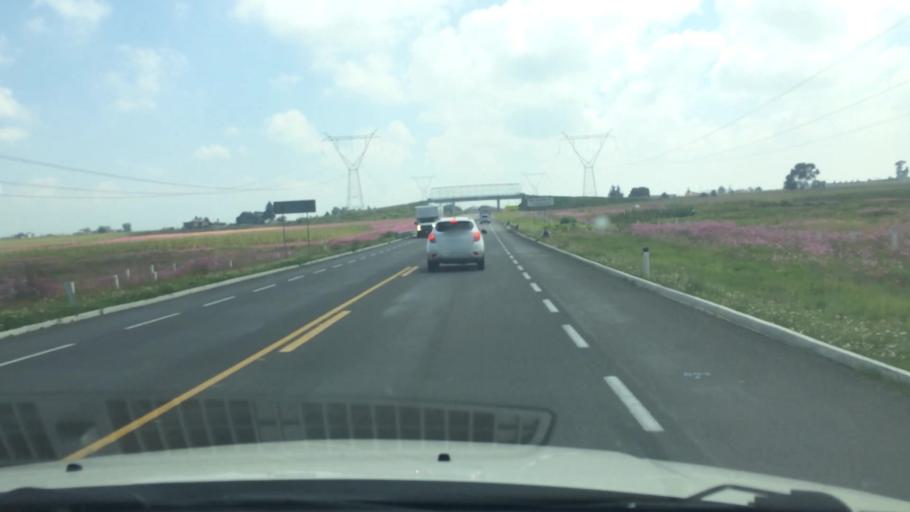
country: MX
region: Mexico
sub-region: Toluca
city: Sebastian Lerdo de Tejada
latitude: 19.3878
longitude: -99.7332
